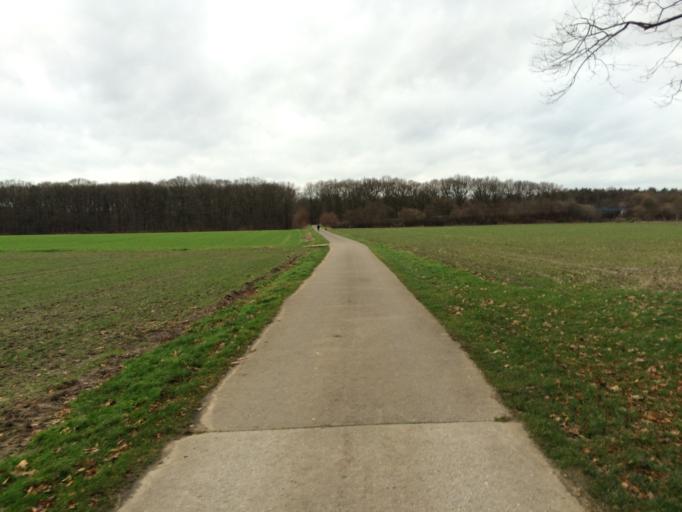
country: DE
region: North Rhine-Westphalia
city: Dorsten
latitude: 51.6787
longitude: 7.0243
